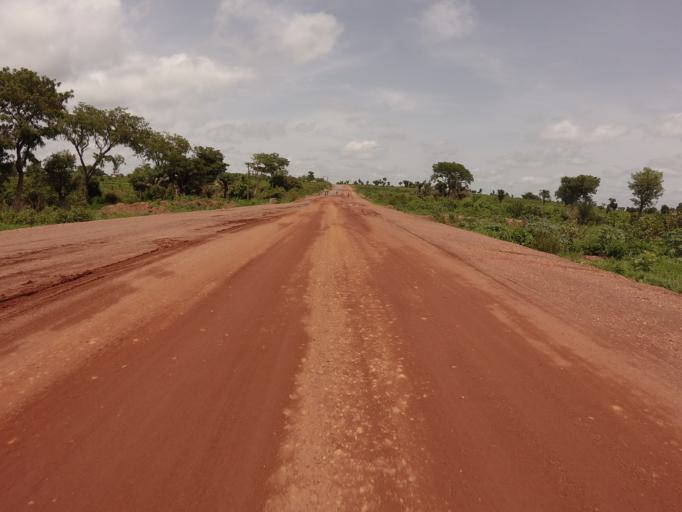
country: GH
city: Kpandae
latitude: 8.6255
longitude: 0.2260
